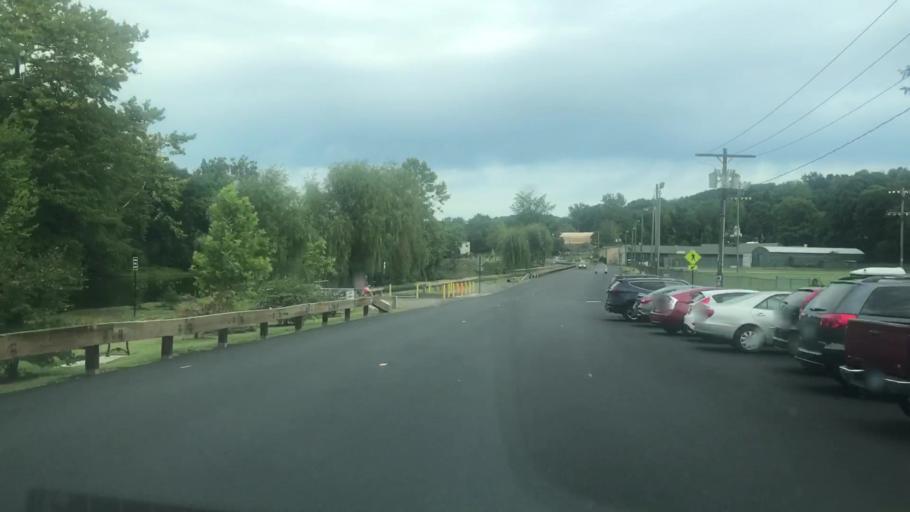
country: US
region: Connecticut
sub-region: Litchfield County
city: New Milford
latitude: 41.5756
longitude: -73.4149
